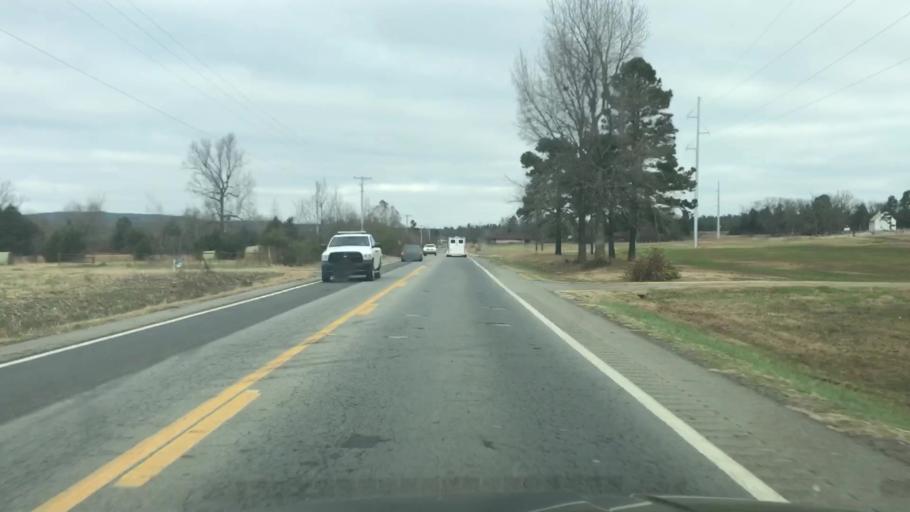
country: US
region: Arkansas
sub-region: Scott County
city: Waldron
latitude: 34.9433
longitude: -94.1031
